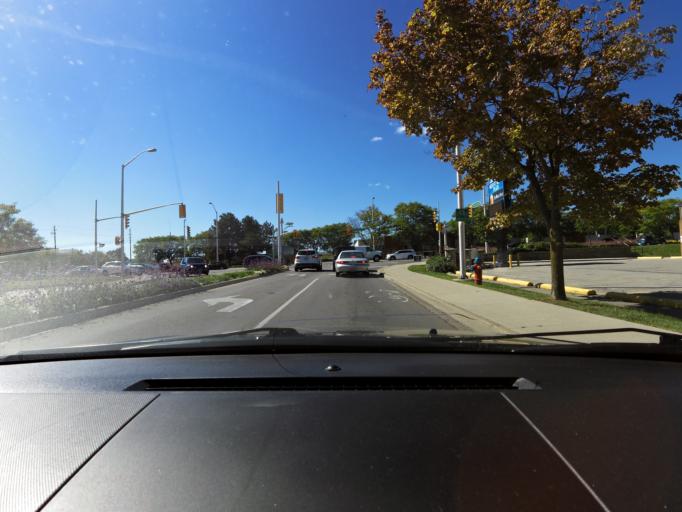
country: CA
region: Ontario
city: Burlington
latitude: 43.3467
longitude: -79.8284
